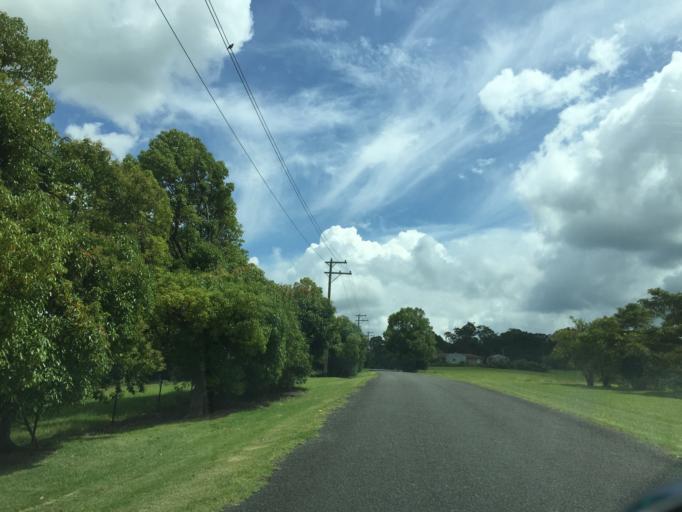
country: AU
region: New South Wales
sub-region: Hornsby Shire
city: Galston
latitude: -33.6564
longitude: 151.0527
